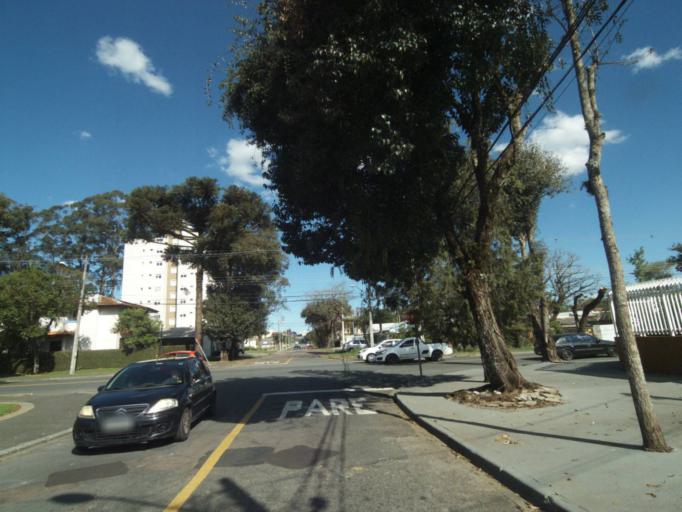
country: BR
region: Parana
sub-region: Curitiba
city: Curitiba
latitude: -25.3854
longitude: -49.2411
